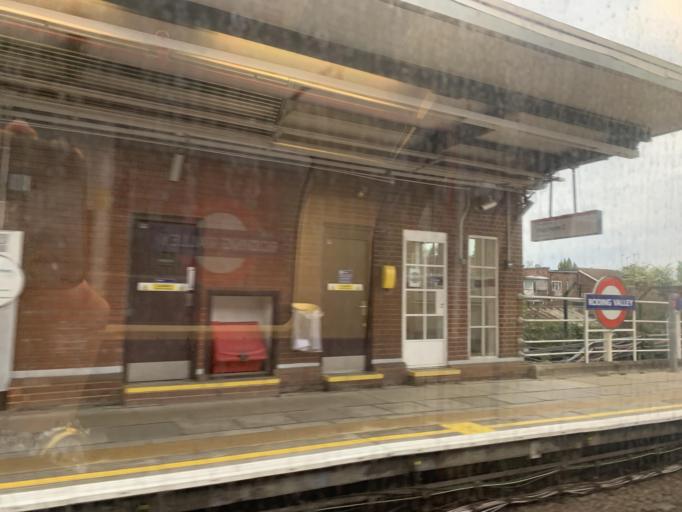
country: GB
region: England
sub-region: Essex
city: Buckhurst Hill
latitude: 51.6172
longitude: 0.0440
